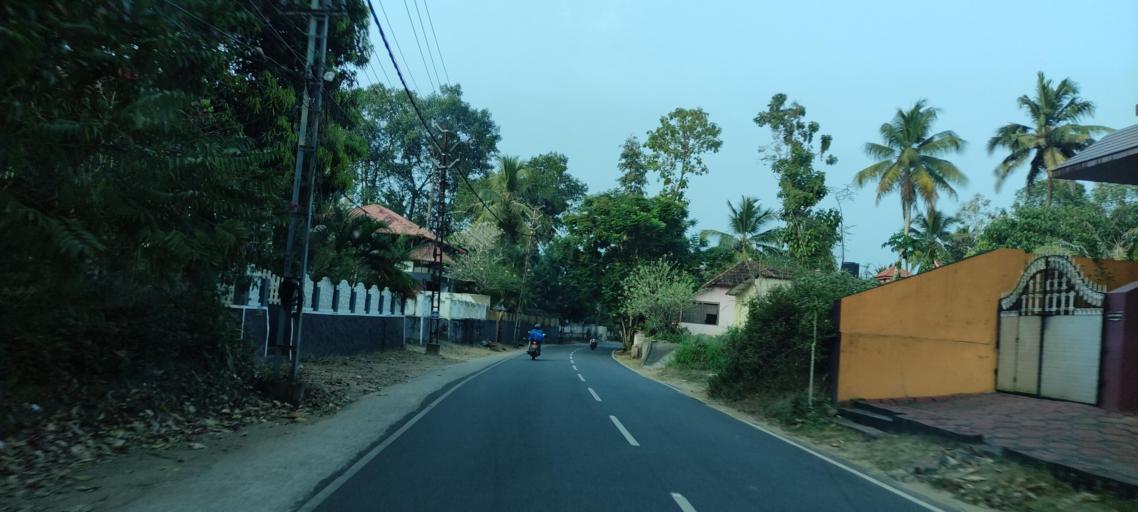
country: IN
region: Kerala
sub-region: Alappuzha
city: Mavelikara
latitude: 9.2580
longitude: 76.5537
